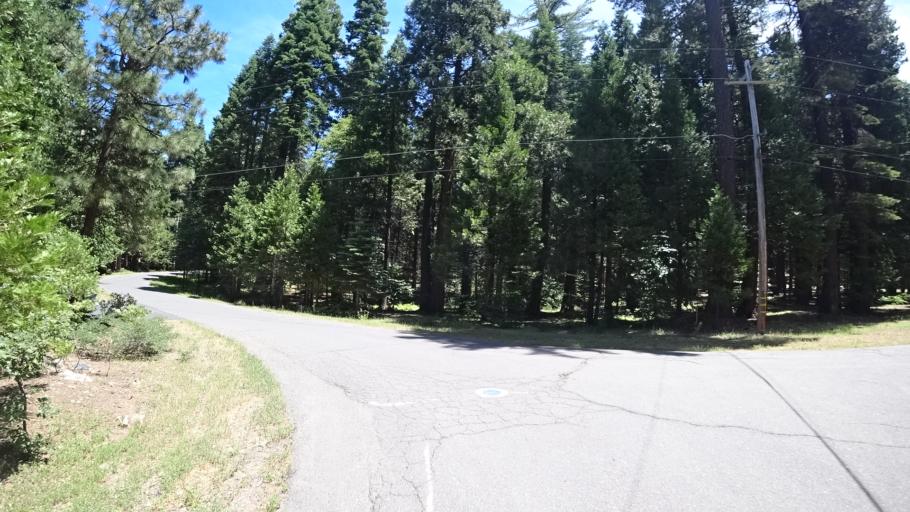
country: US
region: California
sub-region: Calaveras County
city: Arnold
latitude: 38.3177
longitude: -120.2575
